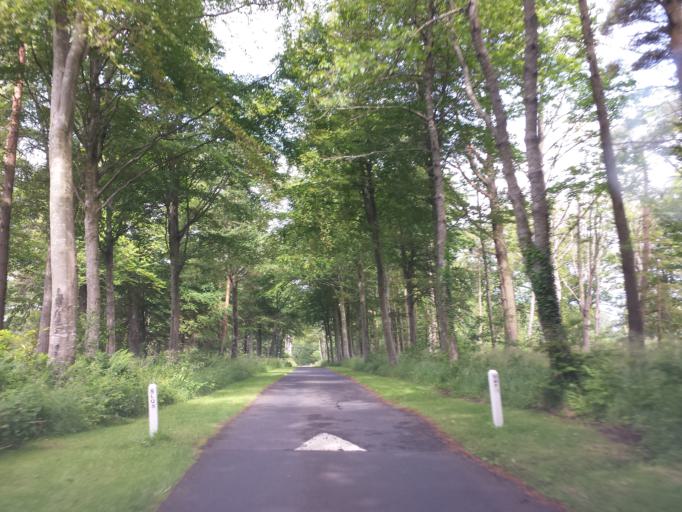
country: GB
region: Scotland
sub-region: South Ayrshire
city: Maybole
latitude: 55.3526
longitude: -4.7776
